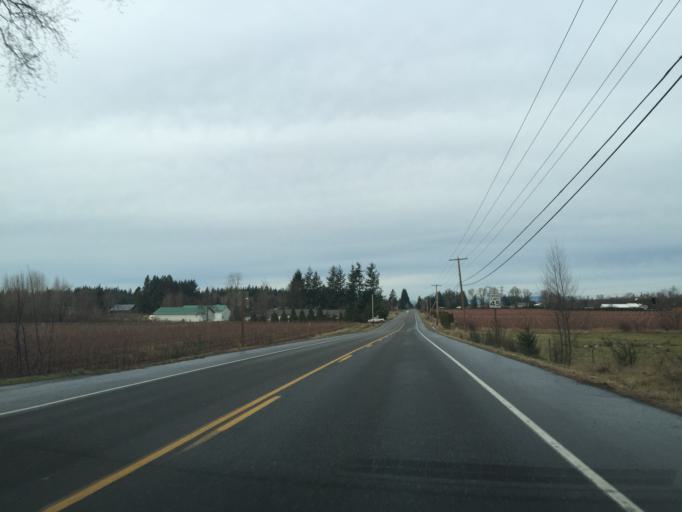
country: US
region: Washington
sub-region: Whatcom County
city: Ferndale
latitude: 48.8614
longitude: -122.5409
